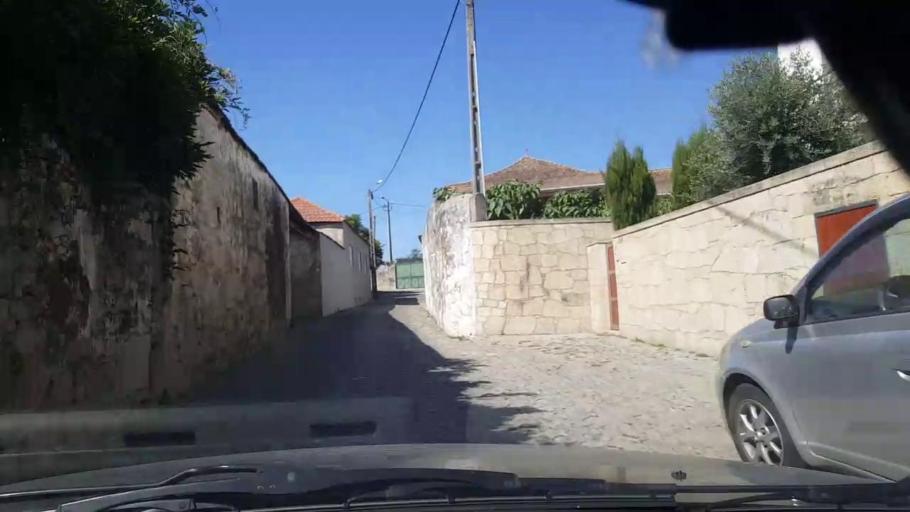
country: PT
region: Porto
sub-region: Maia
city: Gemunde
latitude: 41.3118
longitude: -8.6732
